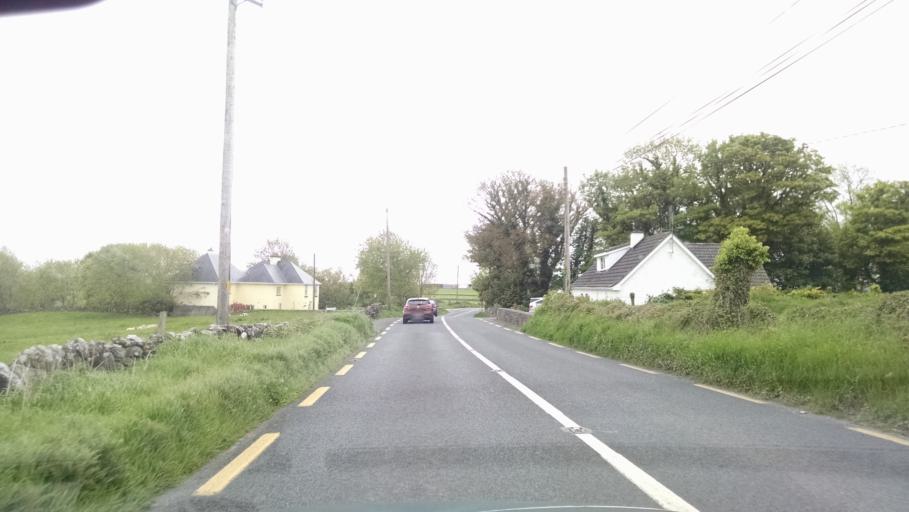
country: IE
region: Connaught
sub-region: County Galway
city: Moycullen
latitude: 53.5001
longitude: -9.0798
